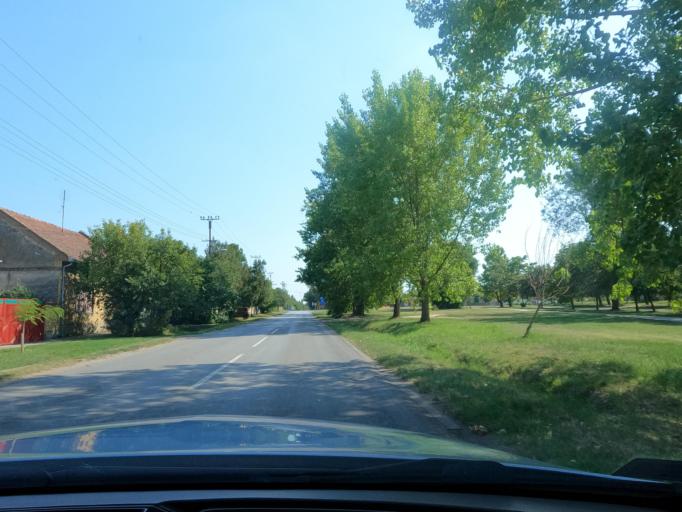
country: RS
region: Autonomna Pokrajina Vojvodina
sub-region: Severnobacki Okrug
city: Backa Topola
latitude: 45.8112
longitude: 19.6441
